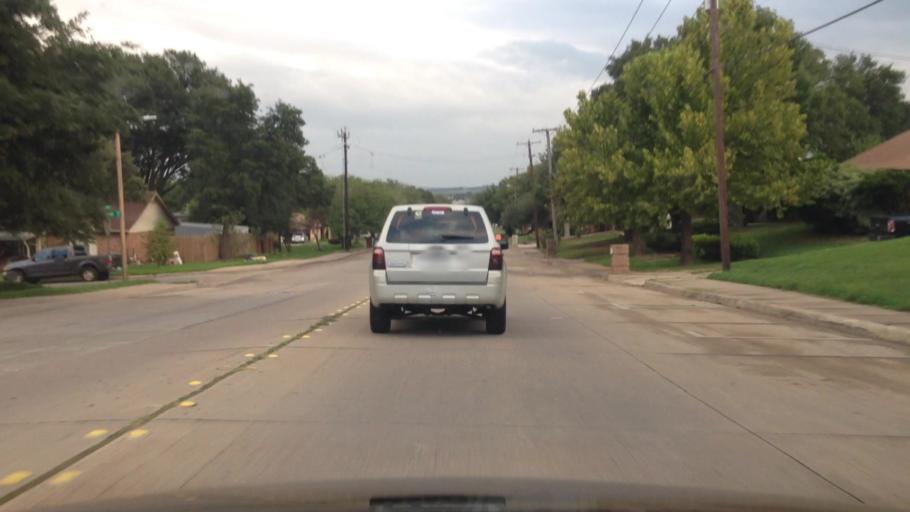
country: US
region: Texas
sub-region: Johnson County
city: Burleson
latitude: 32.5532
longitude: -97.3368
